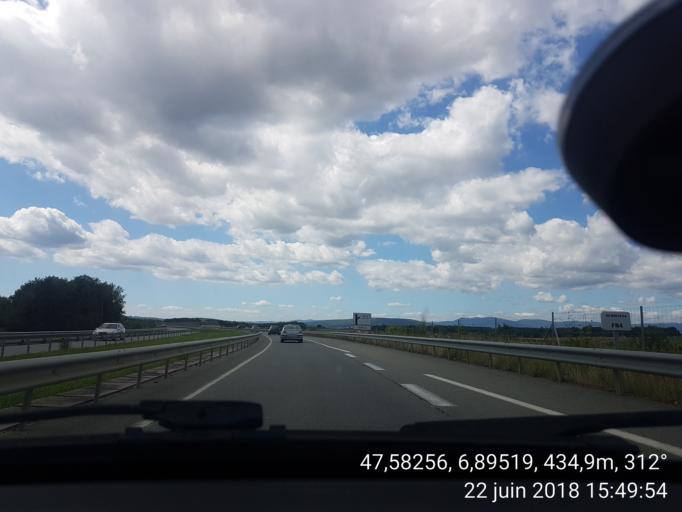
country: FR
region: Franche-Comte
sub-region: Territoire de Belfort
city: Bourogne
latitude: 47.5825
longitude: 6.8953
